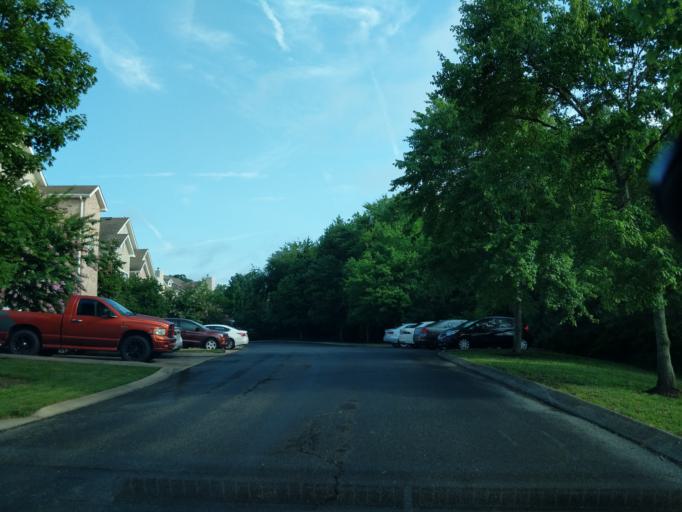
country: US
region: Tennessee
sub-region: Davidson County
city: Goodlettsville
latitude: 36.3039
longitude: -86.6768
